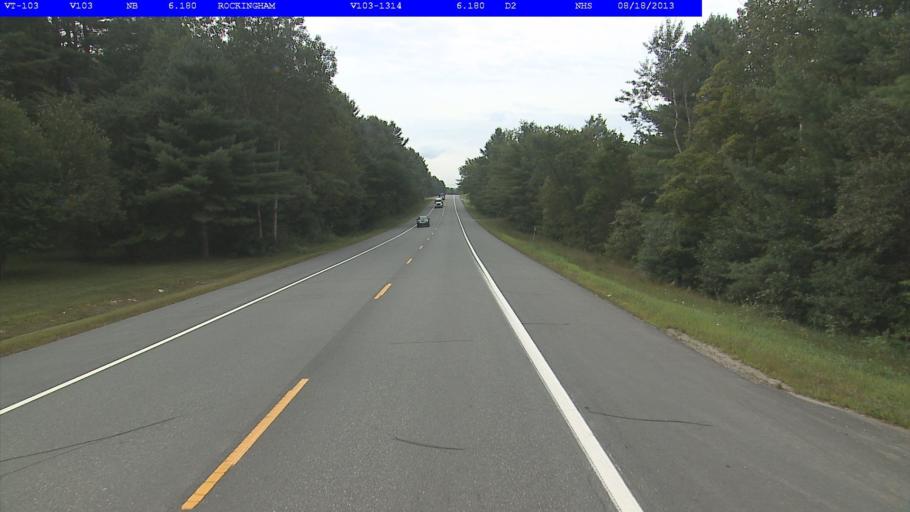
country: US
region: Vermont
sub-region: Windsor County
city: Chester
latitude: 43.2292
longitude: -72.5453
